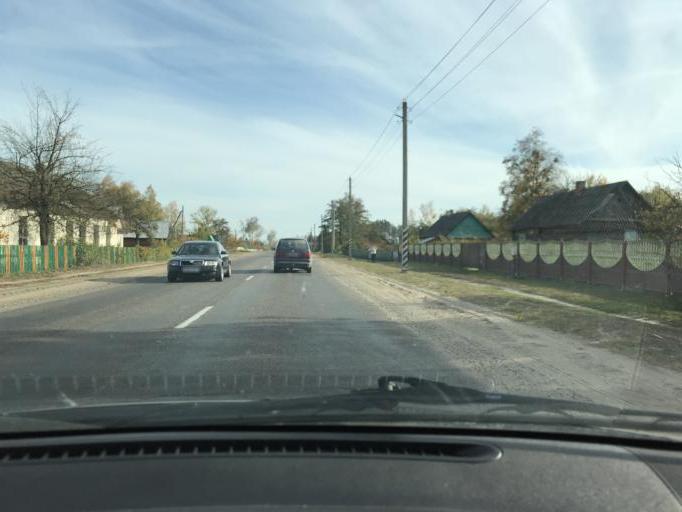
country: BY
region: Brest
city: Asnyezhytsy
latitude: 52.2250
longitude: 26.0264
